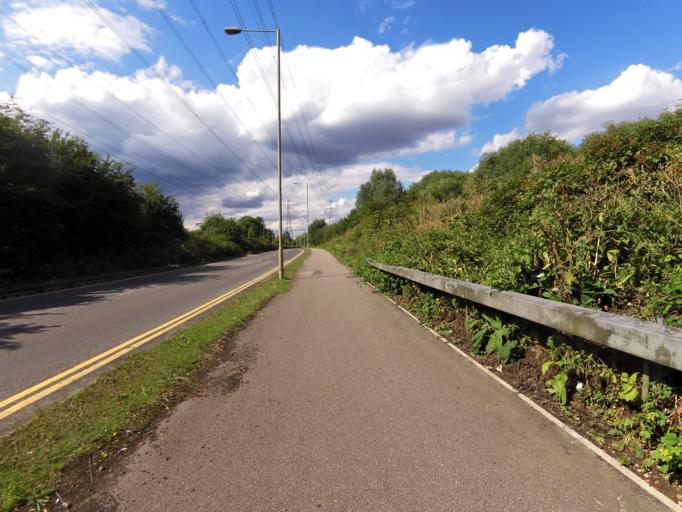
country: GB
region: England
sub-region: Essex
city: Waltham Abbey
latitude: 51.6806
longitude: -0.0106
